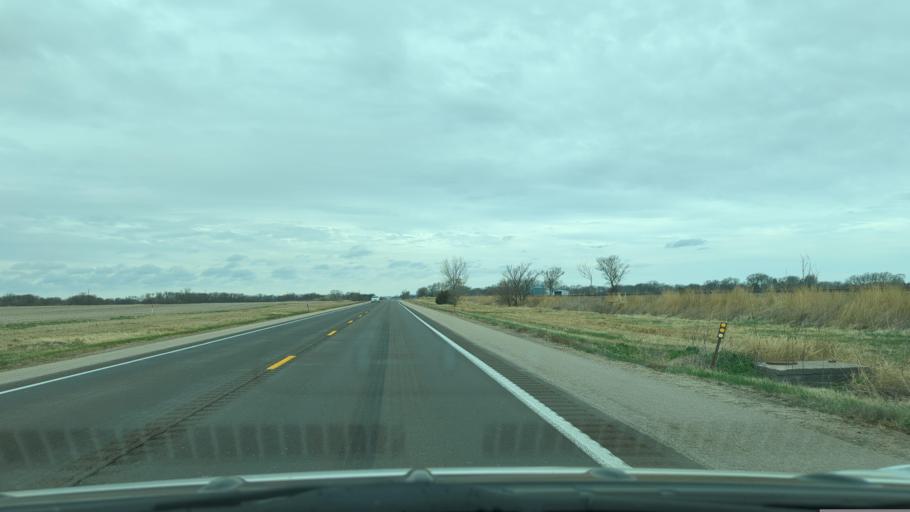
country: US
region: Nebraska
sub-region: Lancaster County
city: Waverly
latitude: 40.9426
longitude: -96.4739
